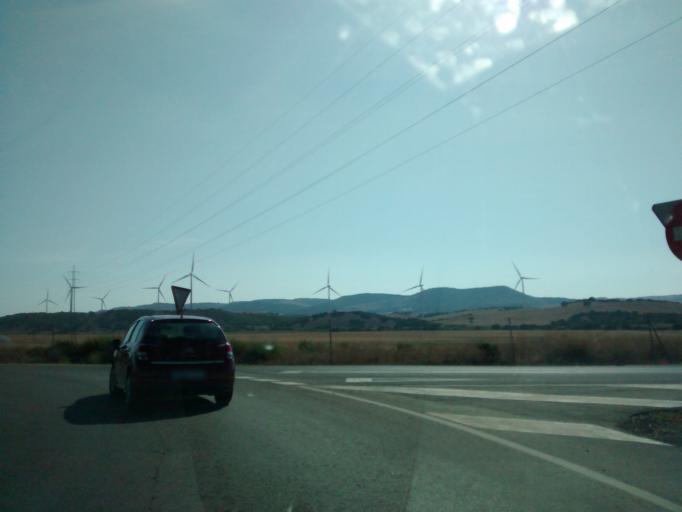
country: ES
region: Andalusia
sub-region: Provincia de Cadiz
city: Conil de la Frontera
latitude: 36.2925
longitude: -6.0556
